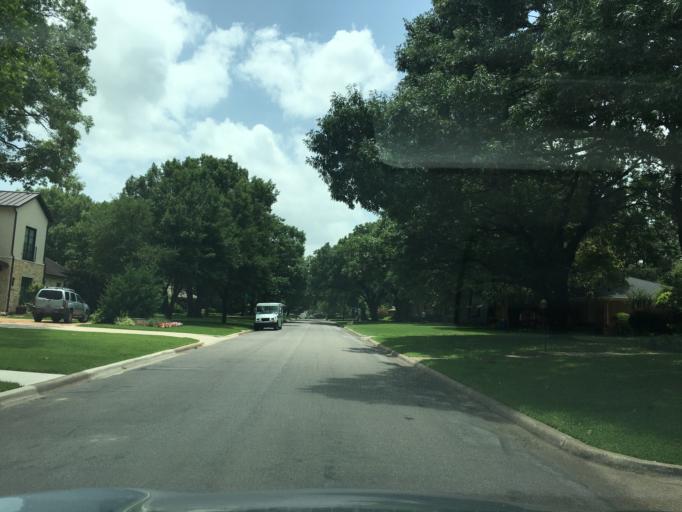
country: US
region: Texas
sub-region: Dallas County
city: University Park
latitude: 32.9059
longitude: -96.8004
